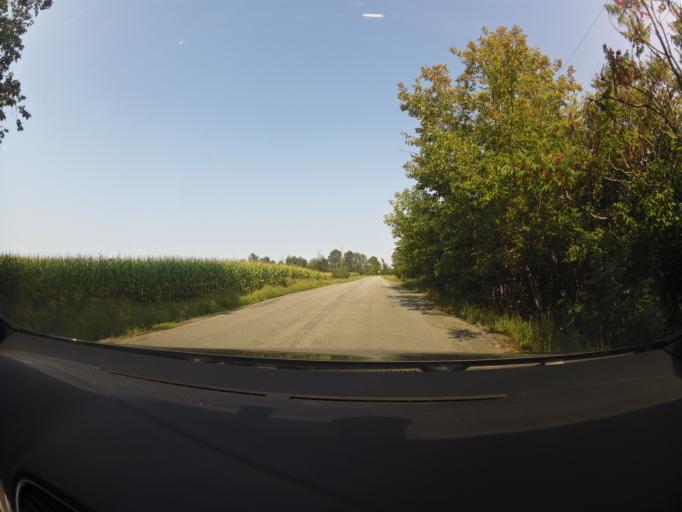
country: CA
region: Ontario
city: Carleton Place
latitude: 45.2840
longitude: -76.1620
